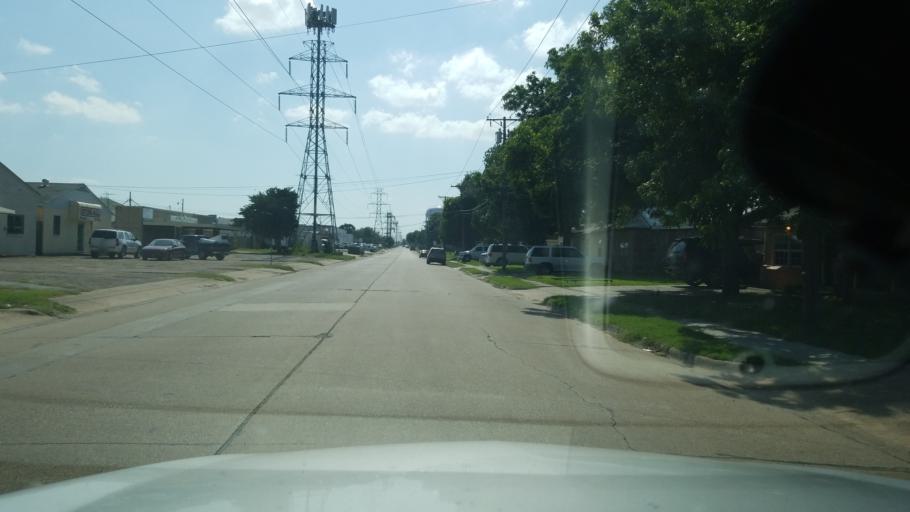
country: US
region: Texas
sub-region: Dallas County
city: Irving
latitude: 32.8162
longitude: -96.9694
